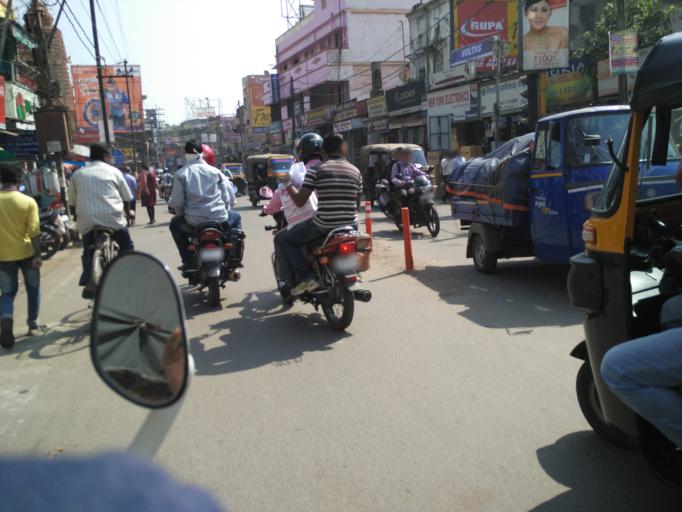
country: IN
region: Odisha
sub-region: Cuttack
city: Cuttack
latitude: 20.4690
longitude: 85.8891
